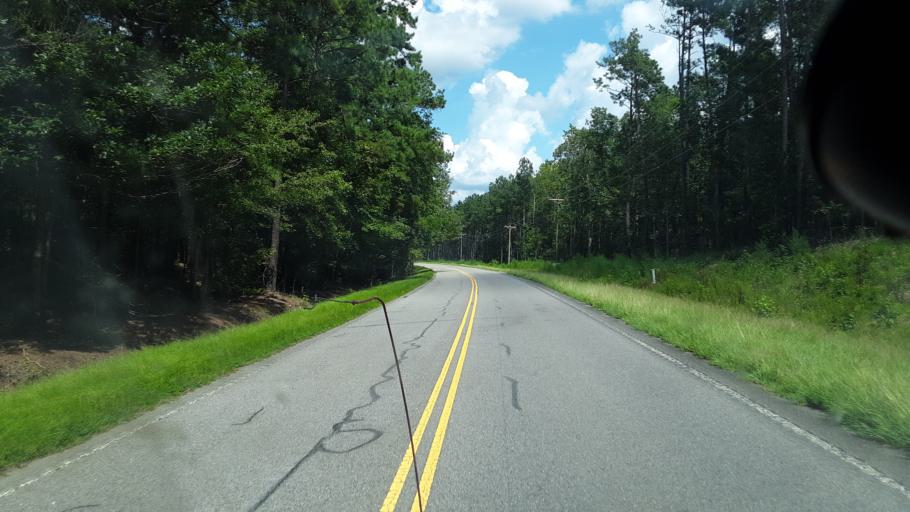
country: US
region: South Carolina
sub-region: Williamsburg County
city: Andrews
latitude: 33.5169
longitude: -79.4973
